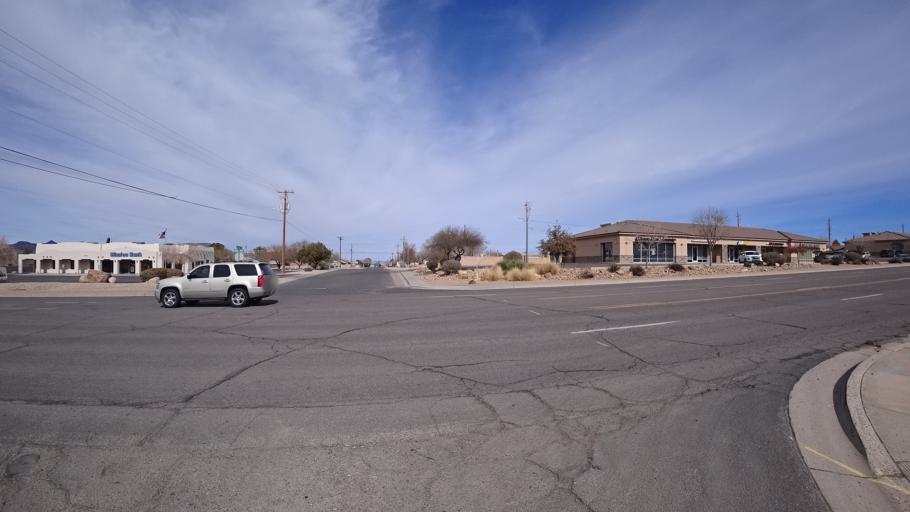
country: US
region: Arizona
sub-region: Mohave County
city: Kingman
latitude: 35.1912
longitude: -114.0203
